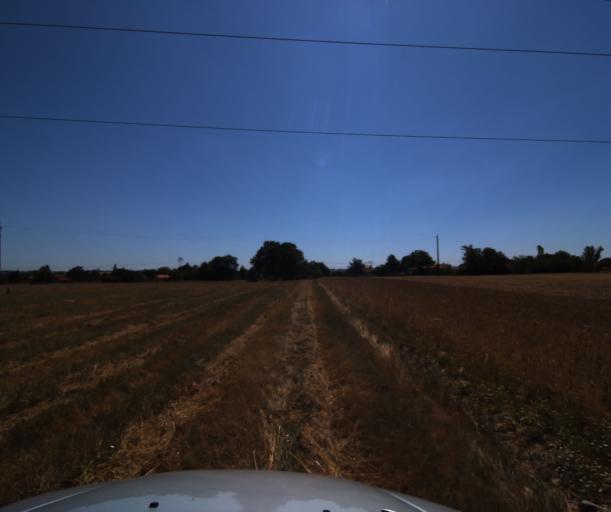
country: FR
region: Midi-Pyrenees
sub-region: Departement de la Haute-Garonne
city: Muret
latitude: 43.4549
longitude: 1.3689
